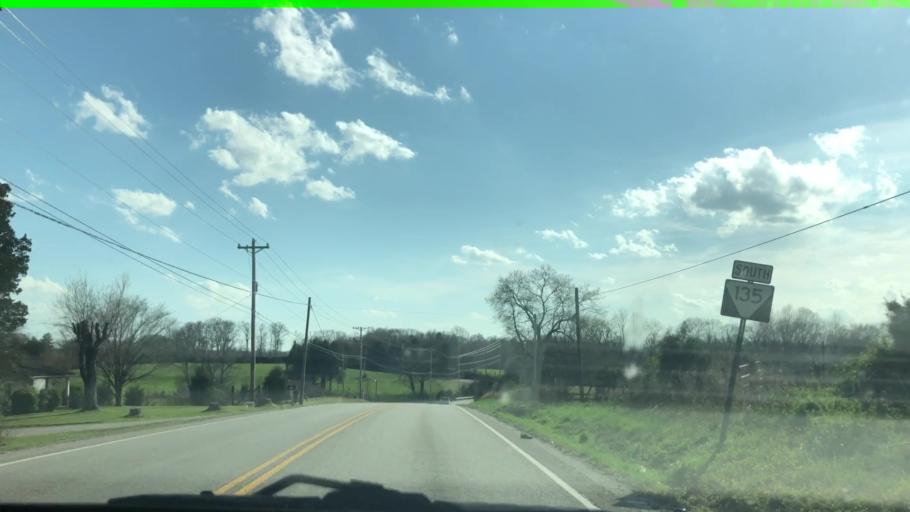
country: US
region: Tennessee
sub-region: Putnam County
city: Baxter
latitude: 36.0908
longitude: -85.5827
